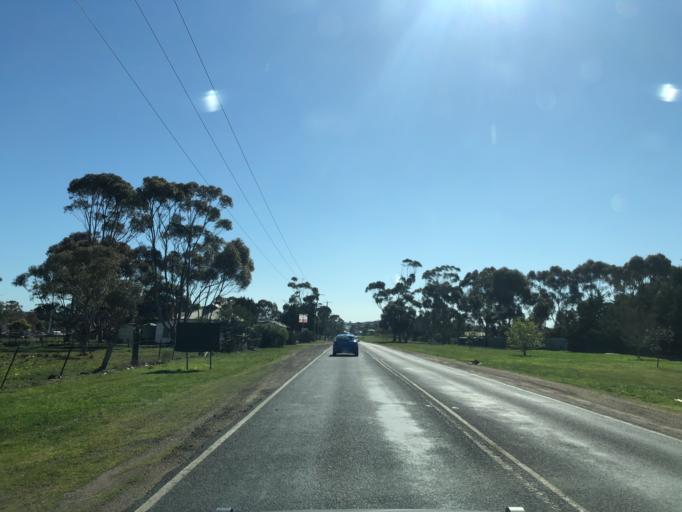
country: AU
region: Victoria
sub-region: Hume
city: Diggers Rest
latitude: -37.6322
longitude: 144.7244
